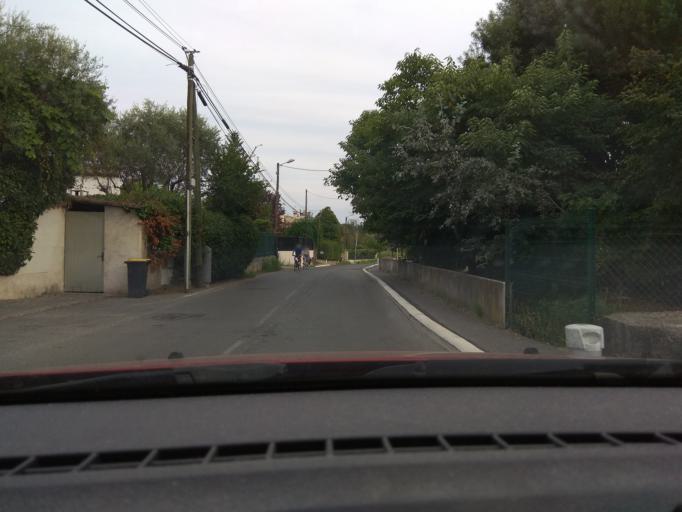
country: FR
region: Provence-Alpes-Cote d'Azur
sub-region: Departement des Alpes-Maritimes
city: La Colle-sur-Loup
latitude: 43.6769
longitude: 7.1087
